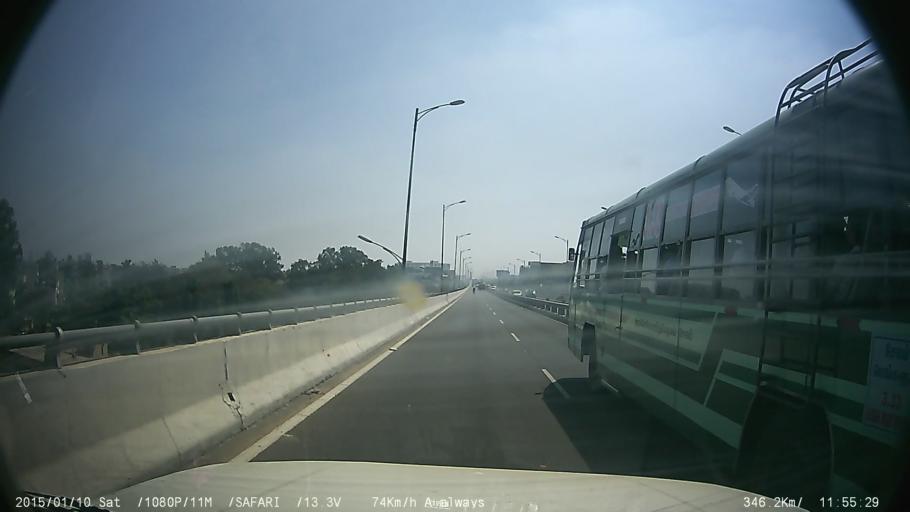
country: IN
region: Karnataka
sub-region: Bangalore Urban
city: Bangalore
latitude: 12.8728
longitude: 77.6512
